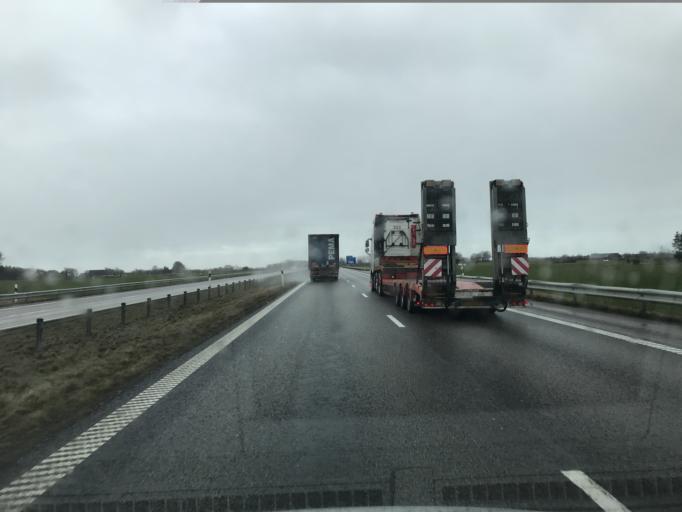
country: SE
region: Skane
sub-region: Angelholms Kommun
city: AEngelholm
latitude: 56.2068
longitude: 12.8761
